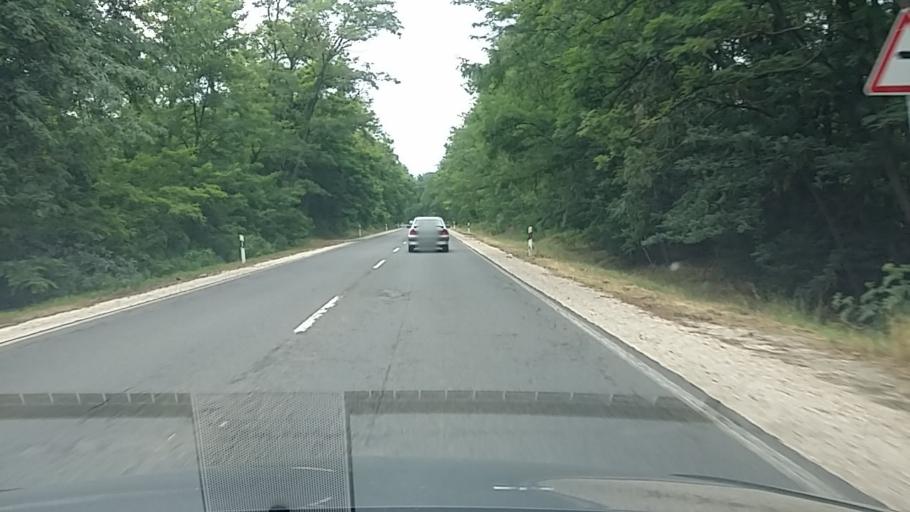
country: HU
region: Pest
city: Hernad
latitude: 47.1600
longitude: 19.3835
